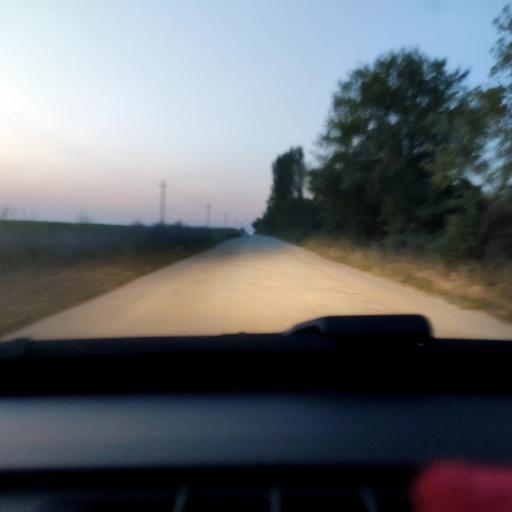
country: RU
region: Voronezj
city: Podgornoye
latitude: 51.8634
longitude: 39.0986
